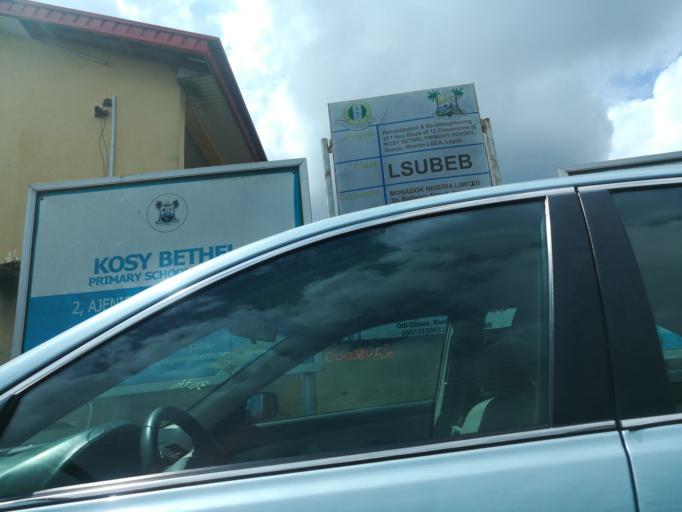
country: NG
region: Lagos
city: Mushin
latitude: 6.5392
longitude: 3.3610
